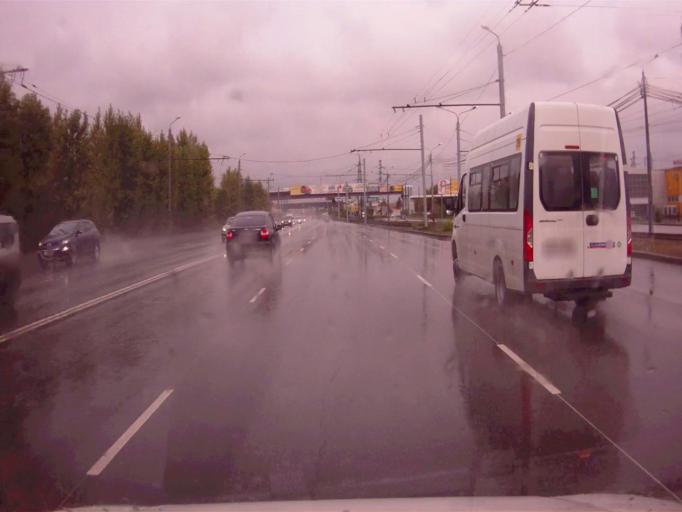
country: RU
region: Chelyabinsk
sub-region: Gorod Chelyabinsk
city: Chelyabinsk
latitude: 55.2016
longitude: 61.3857
